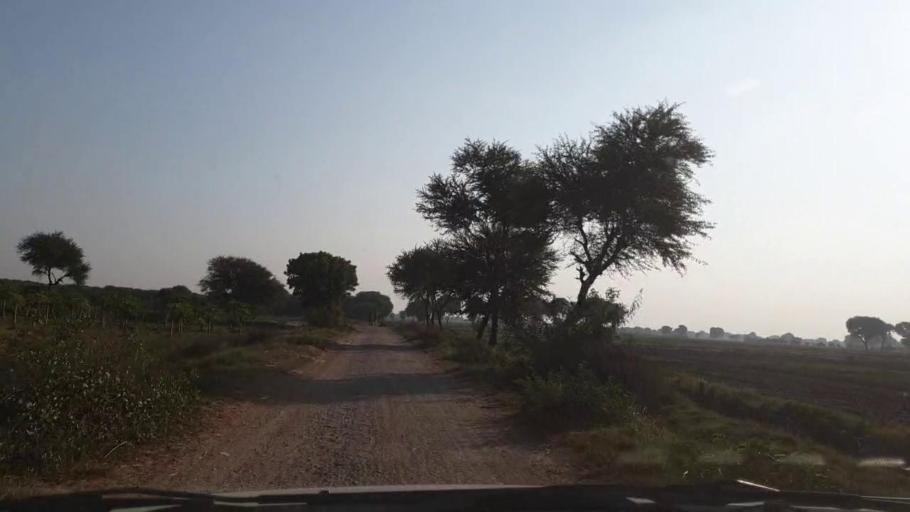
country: PK
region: Sindh
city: Chambar
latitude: 25.2154
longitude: 68.6857
